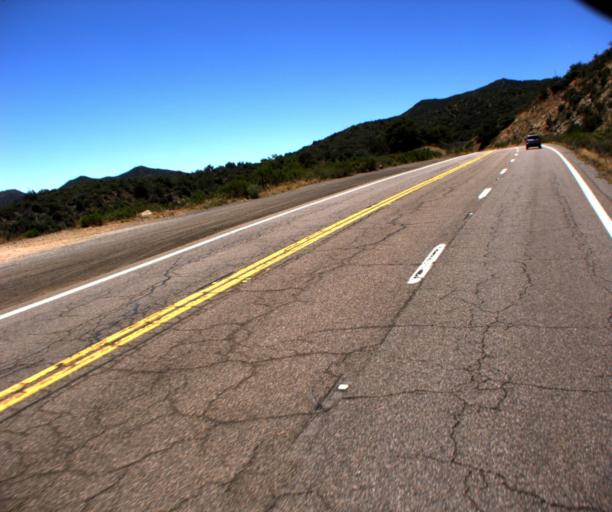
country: US
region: Arizona
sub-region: Gila County
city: Globe
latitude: 33.2634
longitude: -110.7726
